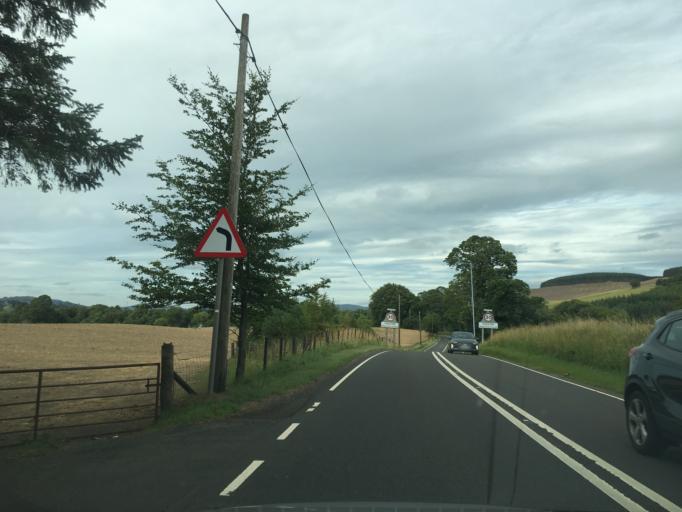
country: GB
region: Scotland
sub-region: South Lanarkshire
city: Biggar
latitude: 55.5871
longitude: -3.5558
